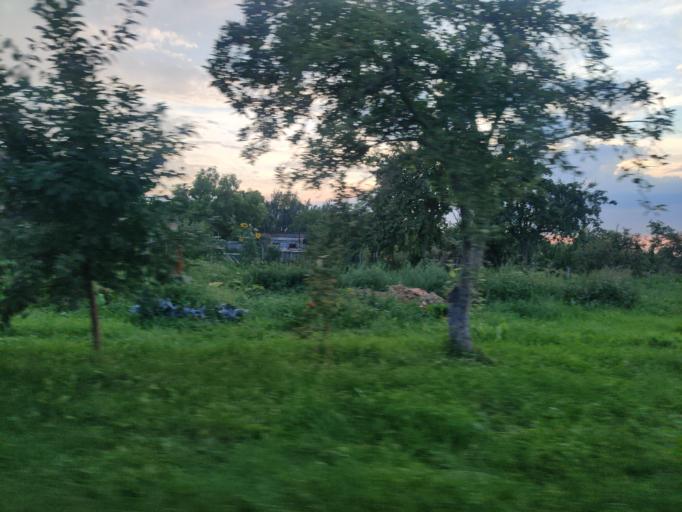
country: PL
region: Greater Poland Voivodeship
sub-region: Konin
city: Konin
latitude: 52.1927
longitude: 18.3138
